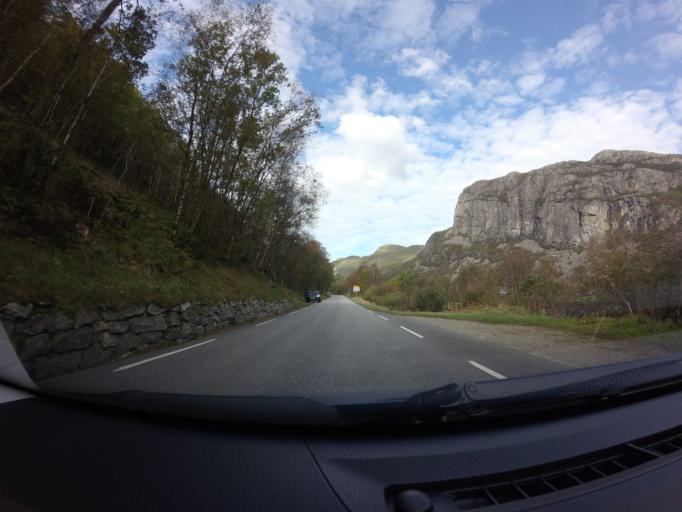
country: NO
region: Rogaland
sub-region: Forsand
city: Forsand
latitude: 58.8035
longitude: 6.2580
